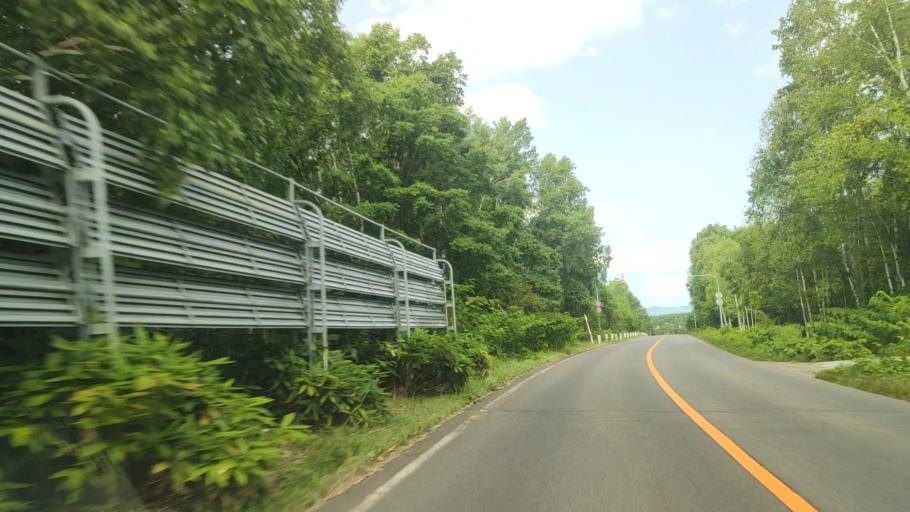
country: JP
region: Hokkaido
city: Nayoro
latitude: 44.2494
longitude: 142.4163
